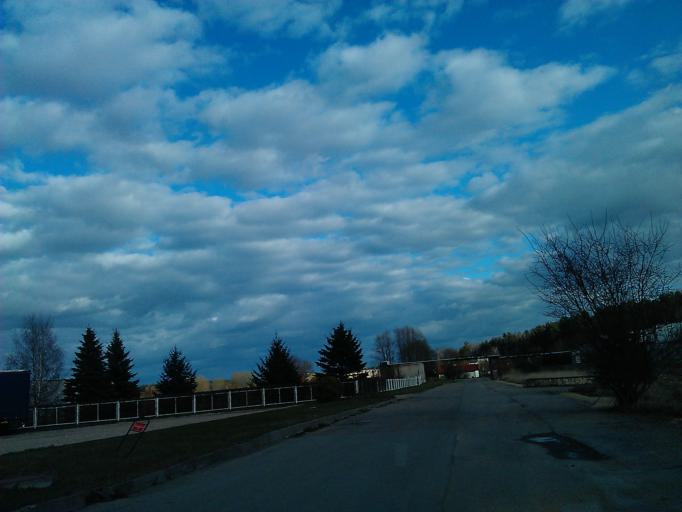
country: LV
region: Adazi
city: Adazi
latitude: 57.0633
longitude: 24.3289
